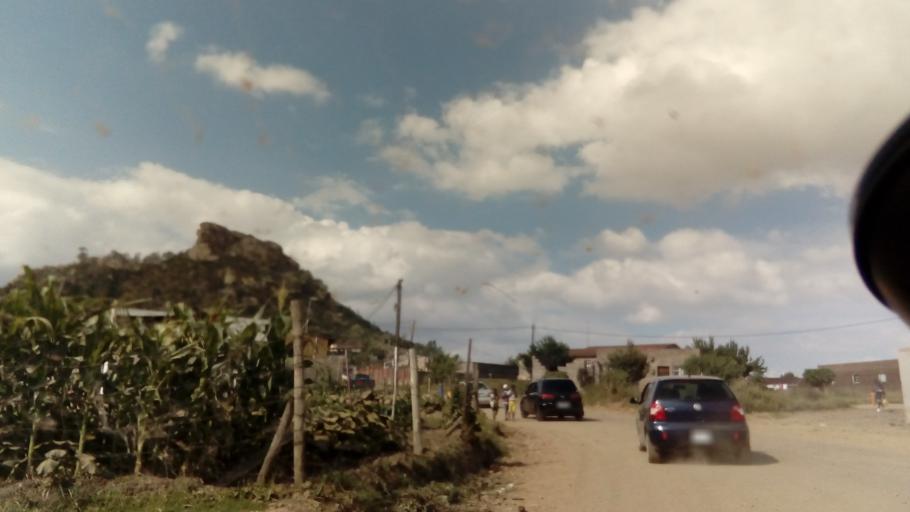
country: LS
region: Maseru
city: Maseru
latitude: -29.3702
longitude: 27.5353
